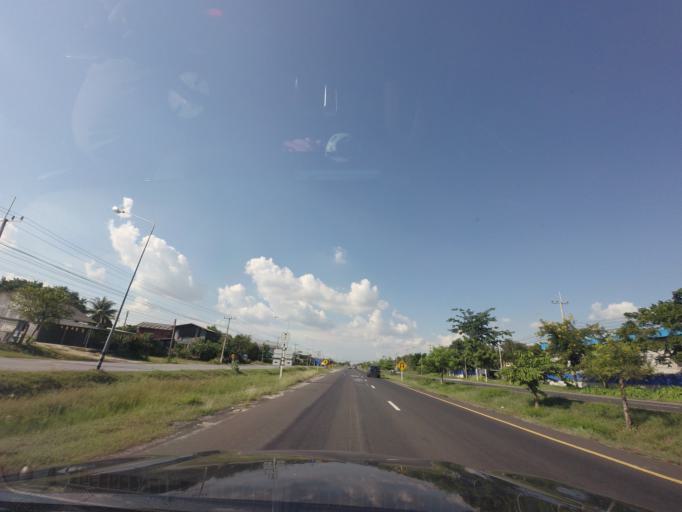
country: TH
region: Nakhon Ratchasima
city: Bua Lai
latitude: 15.6366
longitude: 102.5689
